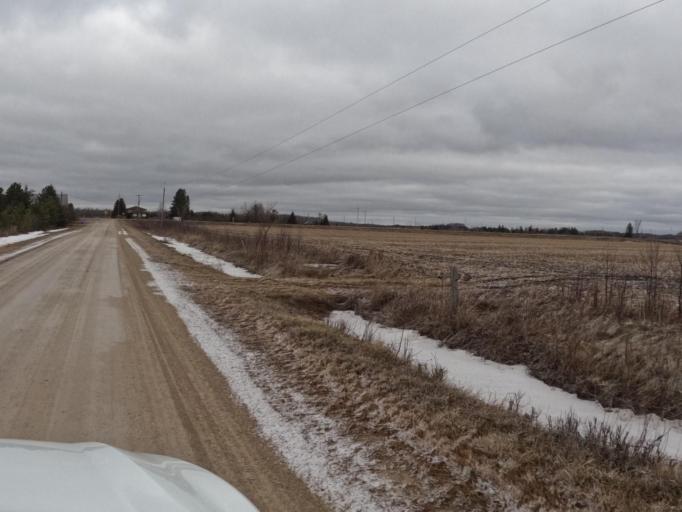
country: CA
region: Ontario
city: Shelburne
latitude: 44.0379
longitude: -80.3728
